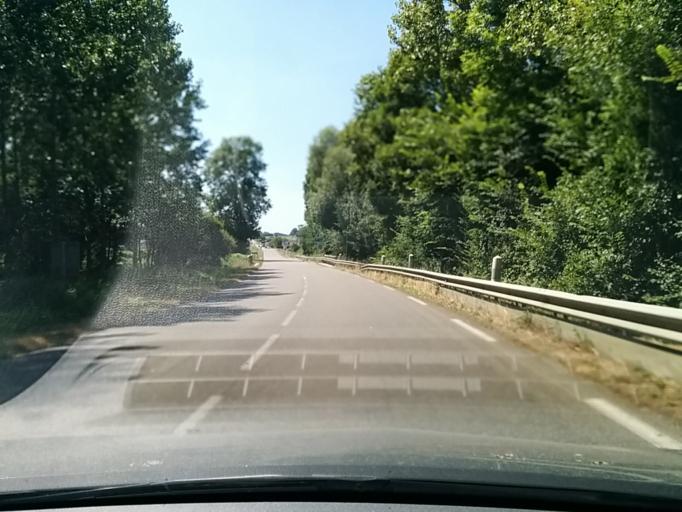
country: FR
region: Midi-Pyrenees
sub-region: Departement du Gers
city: Nogaro
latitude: 43.7506
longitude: -0.0841
